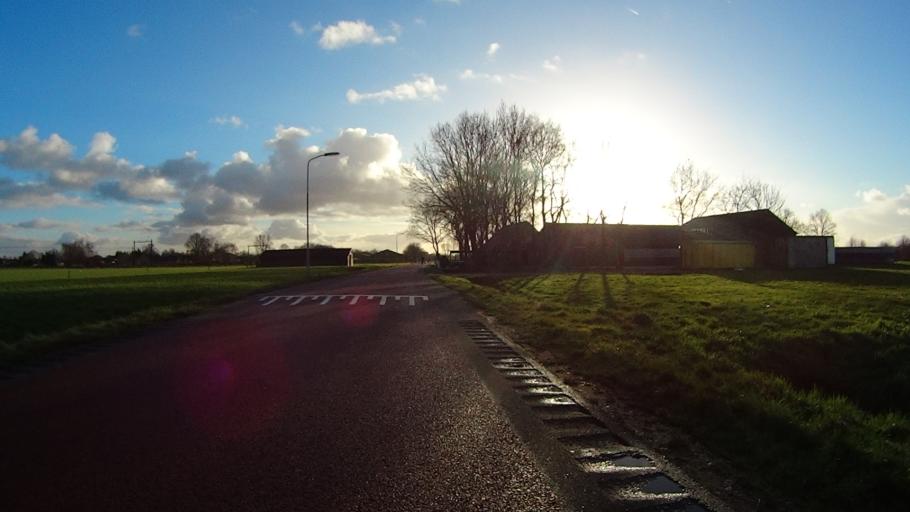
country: NL
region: Gelderland
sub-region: Gemeente Nijkerk
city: Nijkerk
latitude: 52.2041
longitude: 5.4505
